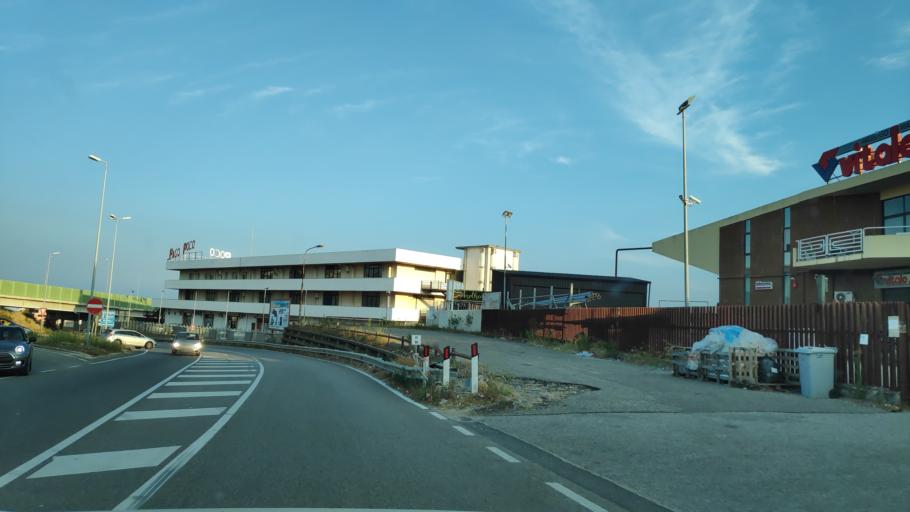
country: IT
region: Calabria
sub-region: Provincia di Catanzaro
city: Martelli-Laganosa
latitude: 38.6780
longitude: 16.5441
